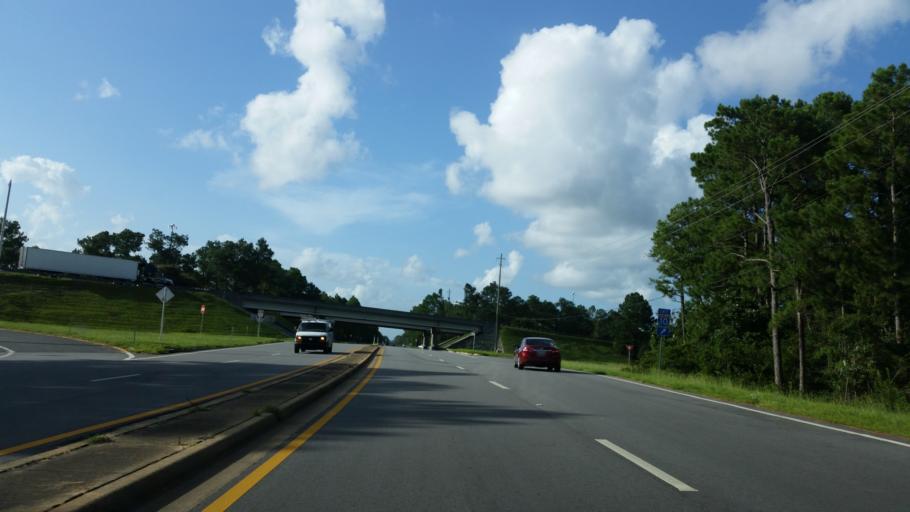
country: US
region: Florida
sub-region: Santa Rosa County
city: Bagdad
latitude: 30.5682
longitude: -87.0315
